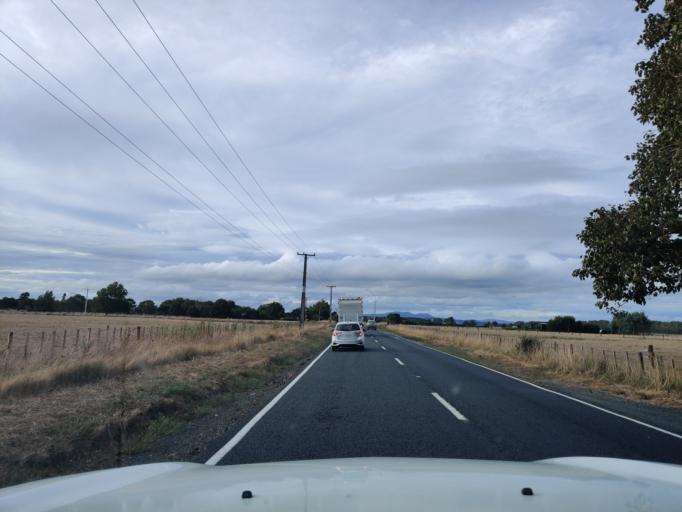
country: NZ
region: Waikato
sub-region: Hamilton City
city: Hamilton
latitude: -37.6881
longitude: 175.3383
